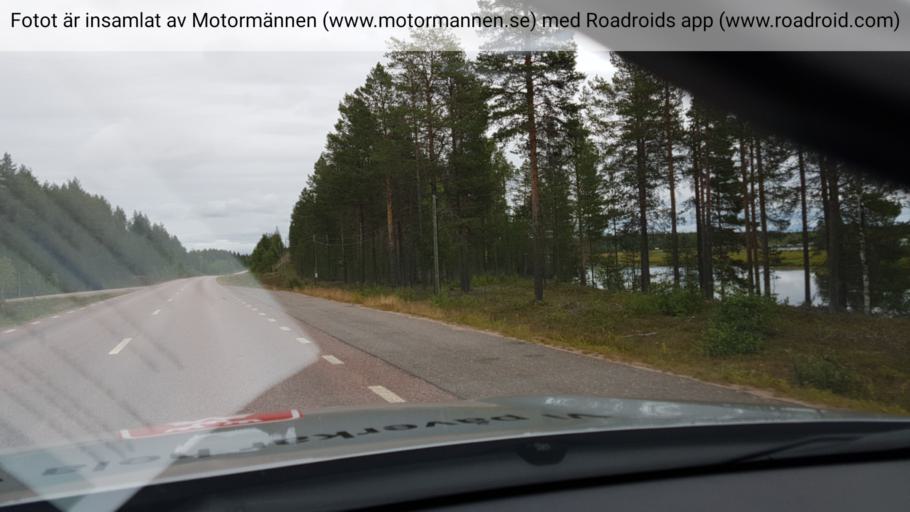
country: SE
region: Norrbotten
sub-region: Overkalix Kommun
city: OEverkalix
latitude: 67.0754
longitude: 22.5292
